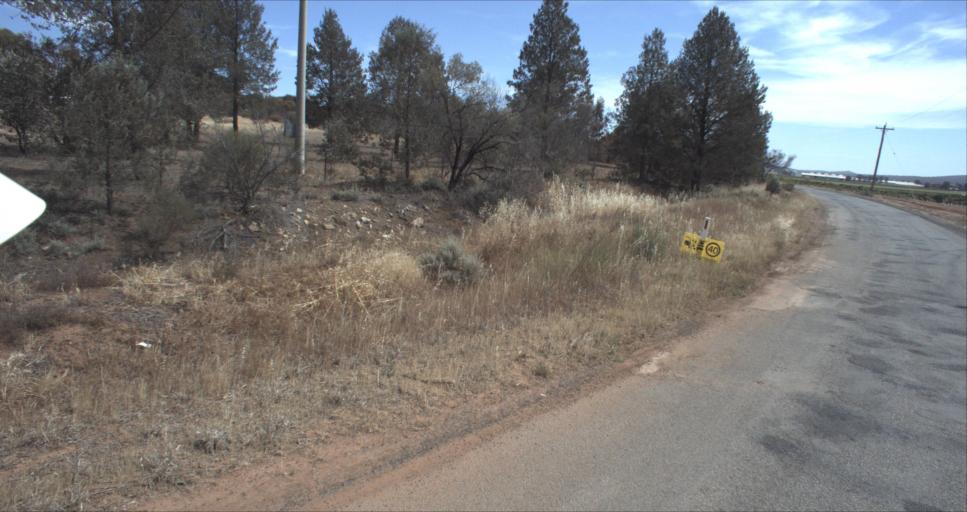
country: AU
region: New South Wales
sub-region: Leeton
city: Leeton
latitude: -34.5695
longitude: 146.4642
